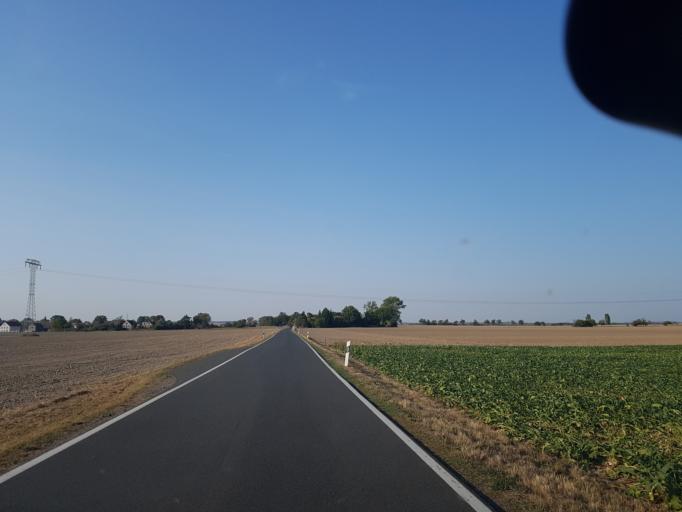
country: DE
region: Saxony
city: Stauchitz
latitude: 51.2833
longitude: 13.1932
